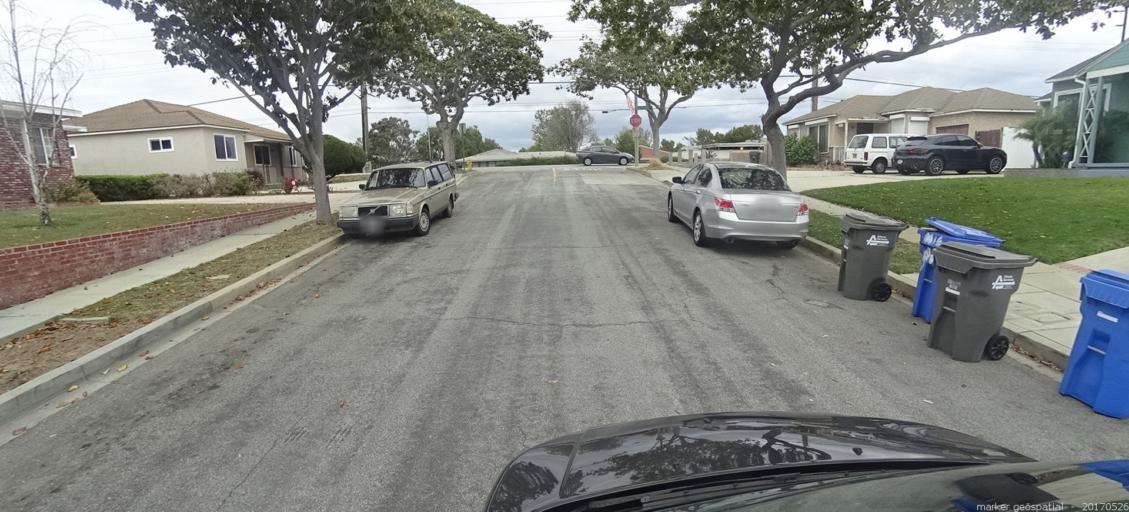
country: US
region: California
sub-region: Los Angeles County
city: Lawndale
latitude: 33.8613
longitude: -118.3618
